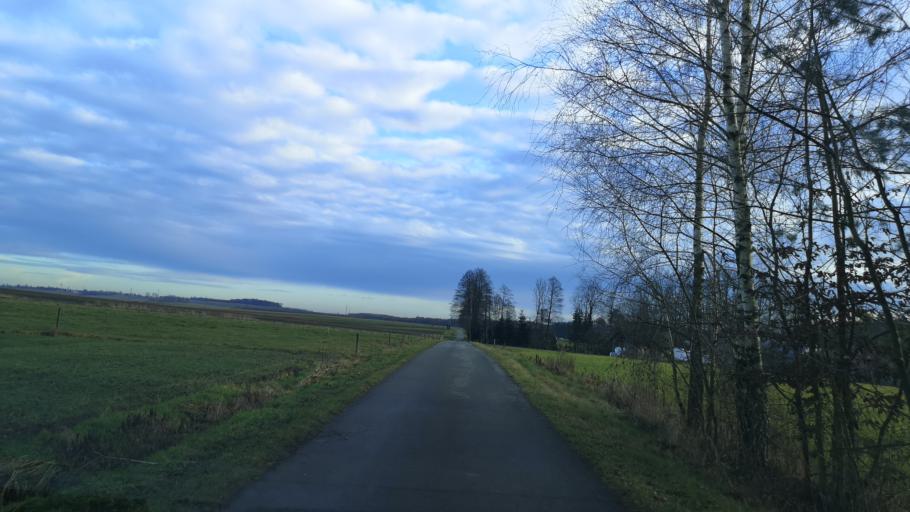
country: PL
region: Subcarpathian Voivodeship
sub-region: Powiat lezajski
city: Piskorowice
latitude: 50.2520
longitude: 22.5753
